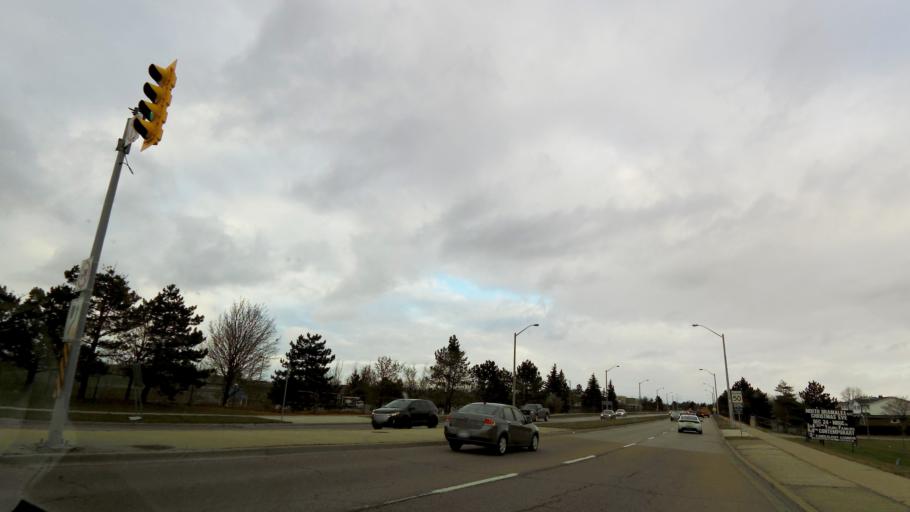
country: CA
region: Ontario
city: Brampton
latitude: 43.7167
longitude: -79.7504
